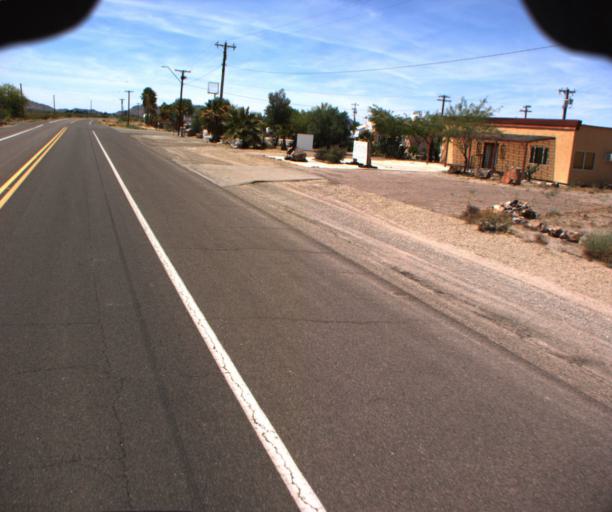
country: US
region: Arizona
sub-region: La Paz County
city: Salome
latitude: 33.7801
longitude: -113.6163
